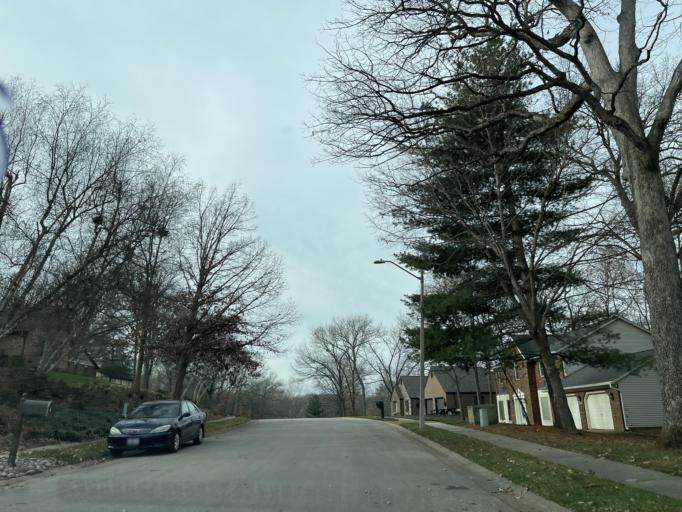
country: US
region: Illinois
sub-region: Sangamon County
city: Leland Grove
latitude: 39.8091
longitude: -89.7274
